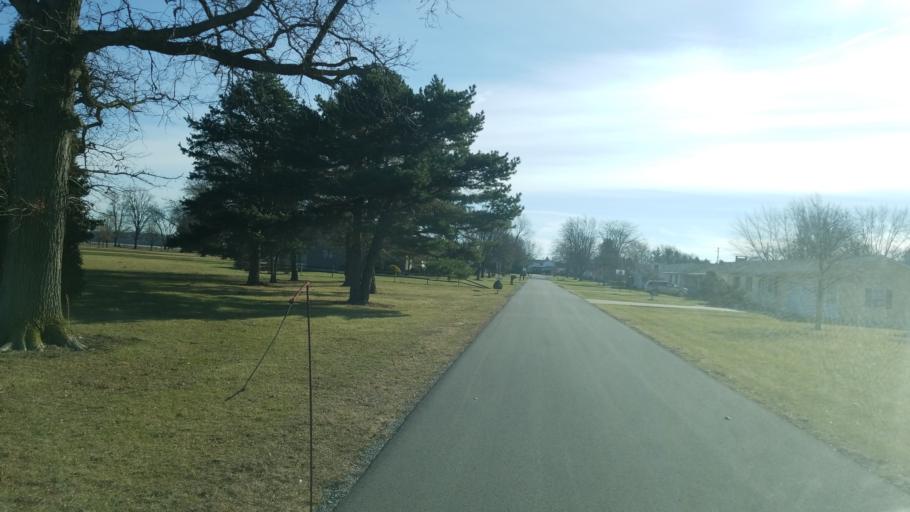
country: US
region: Ohio
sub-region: Putnam County
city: Leipsic
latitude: 41.0999
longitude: -83.9801
